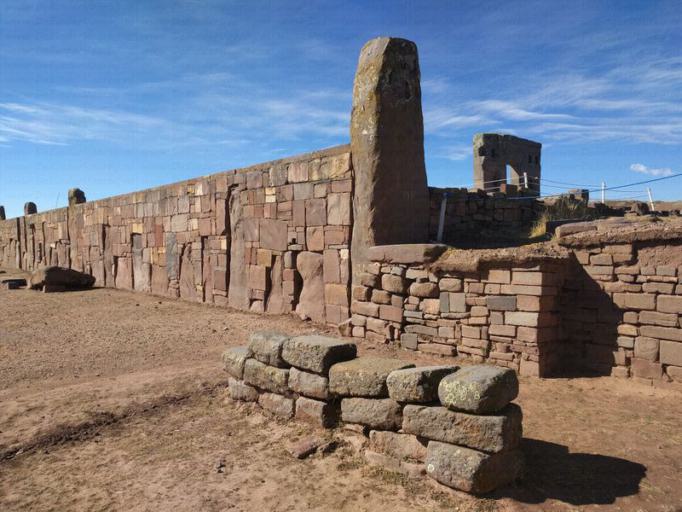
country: BO
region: La Paz
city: Tiahuanaco
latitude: -16.5542
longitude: -68.6740
